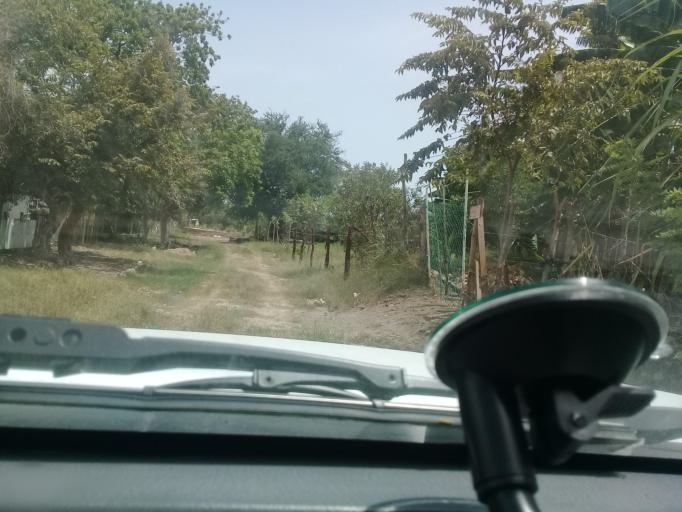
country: MX
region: Veracruz
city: Anahuac
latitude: 22.2250
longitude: -97.8269
